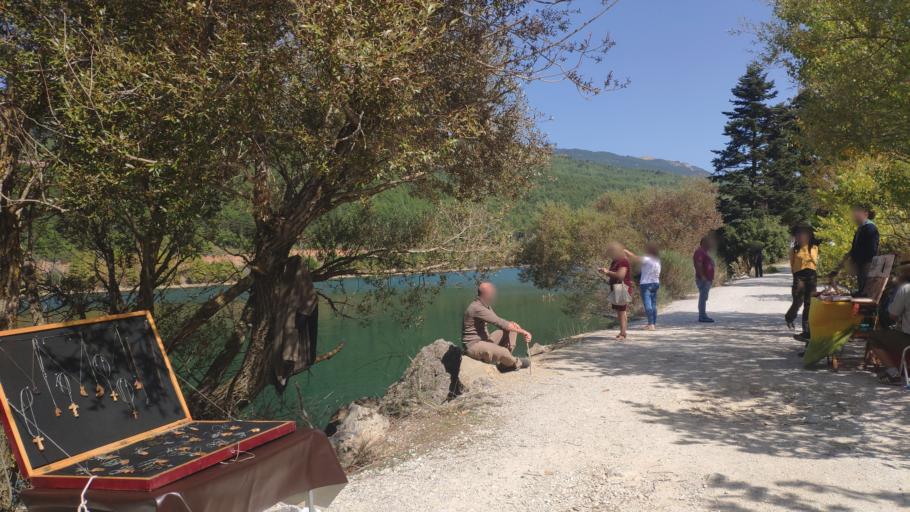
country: GR
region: West Greece
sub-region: Nomos Achaias
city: Kalavryta
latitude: 37.9285
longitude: 22.2866
